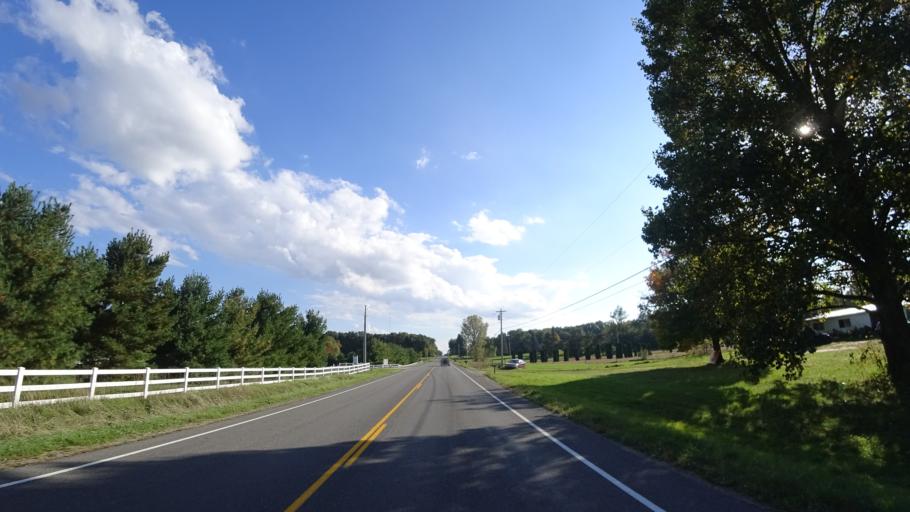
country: US
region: Michigan
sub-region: Saint Joseph County
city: Centreville
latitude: 41.8645
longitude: -85.5066
